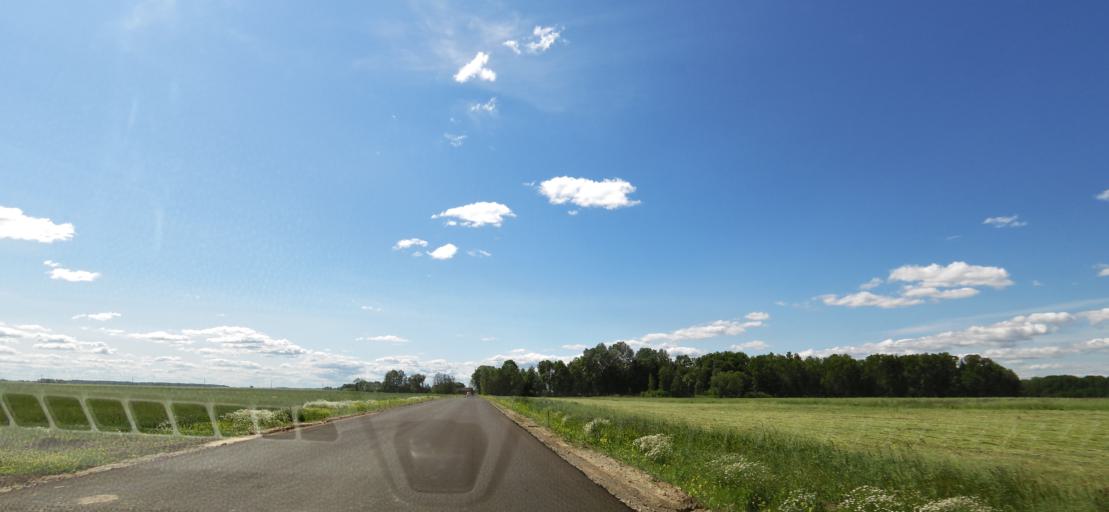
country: LT
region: Panevezys
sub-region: Birzai
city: Birzai
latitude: 56.2925
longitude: 24.6057
